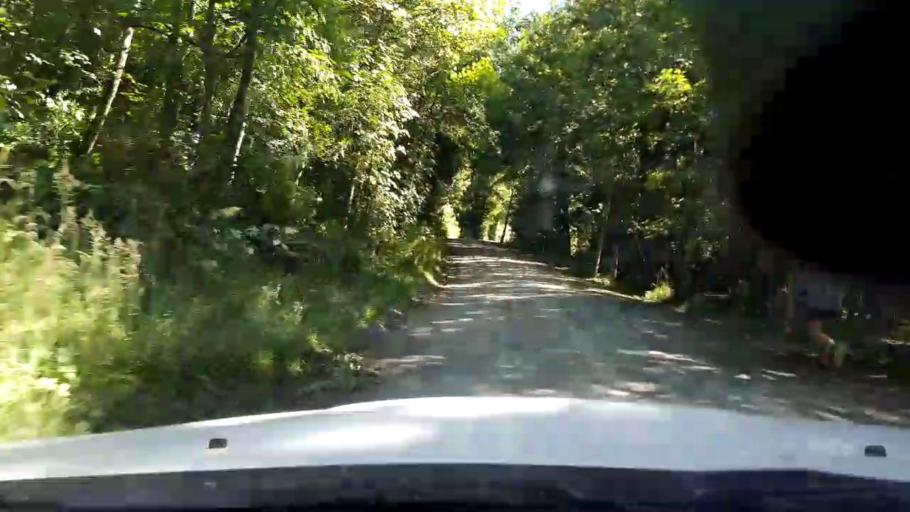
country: NZ
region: Canterbury
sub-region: Timaru District
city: Pleasant Point
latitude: -44.0238
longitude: 170.7438
